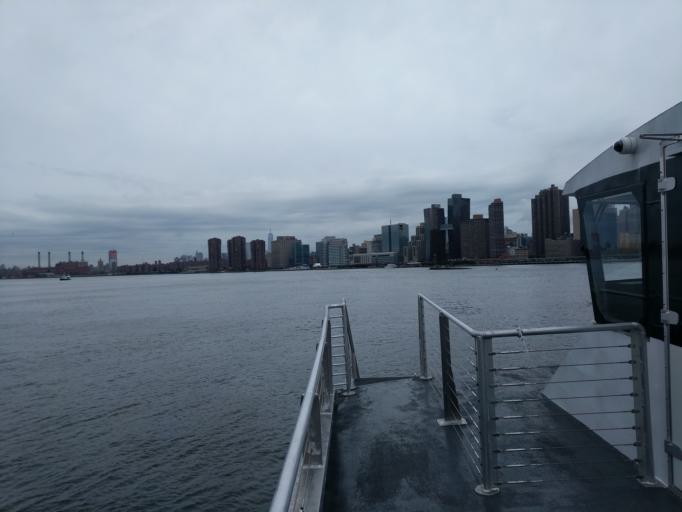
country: US
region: New York
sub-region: Queens County
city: Long Island City
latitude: 40.7483
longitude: -73.9585
